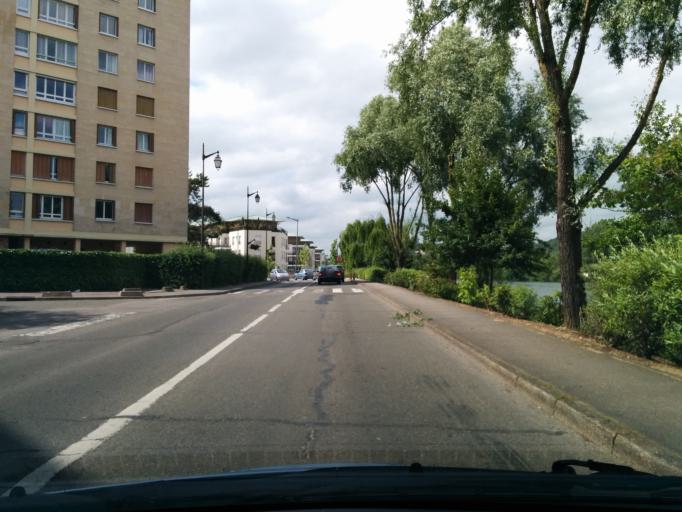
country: FR
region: Ile-de-France
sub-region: Departement des Yvelines
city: Mantes-la-Jolie
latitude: 48.9934
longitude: 1.7186
